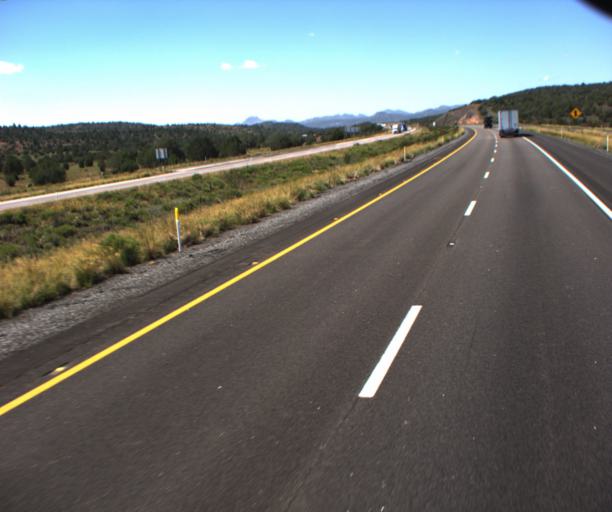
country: US
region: Arizona
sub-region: Mohave County
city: Peach Springs
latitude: 35.2047
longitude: -113.2991
